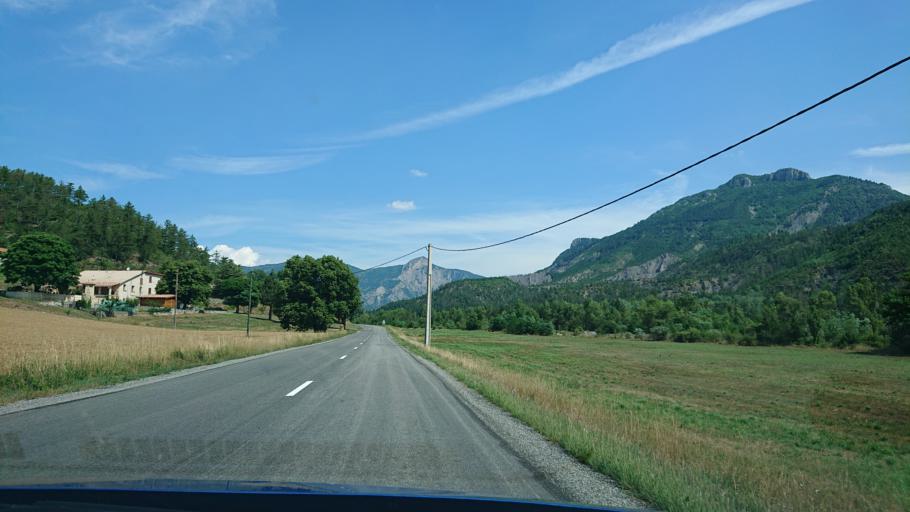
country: FR
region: Provence-Alpes-Cote d'Azur
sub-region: Departement des Hautes-Alpes
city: Tallard
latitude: 44.3119
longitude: 6.0355
